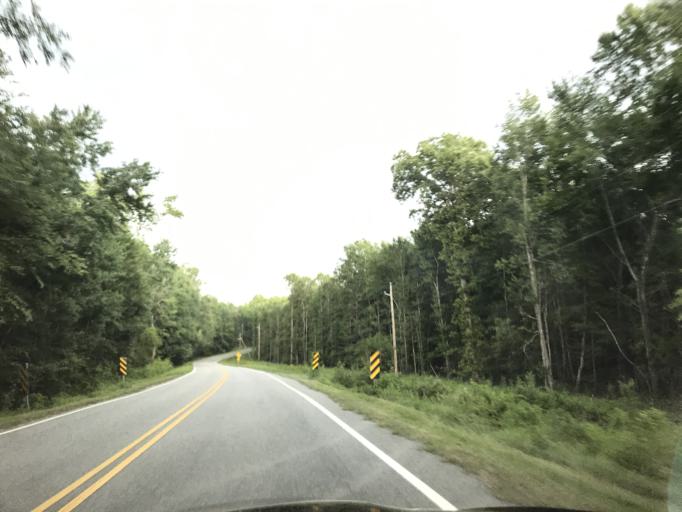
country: US
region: North Carolina
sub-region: Johnston County
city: Four Oaks
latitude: 35.5296
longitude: -78.4373
